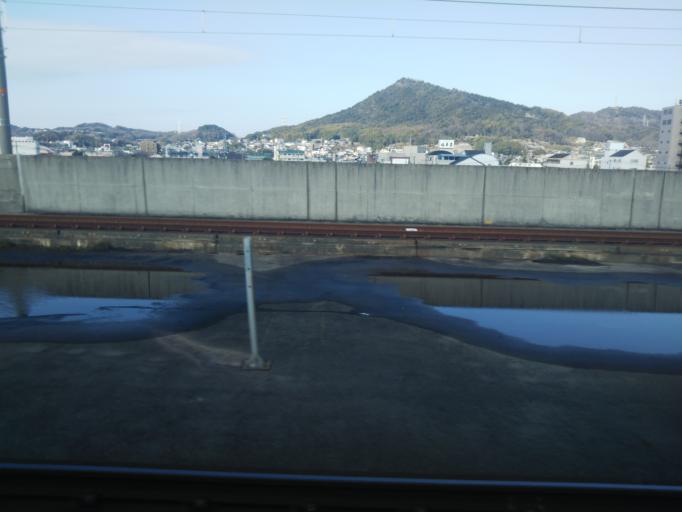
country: JP
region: Okayama
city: Kurashiki
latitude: 34.4611
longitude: 133.8074
